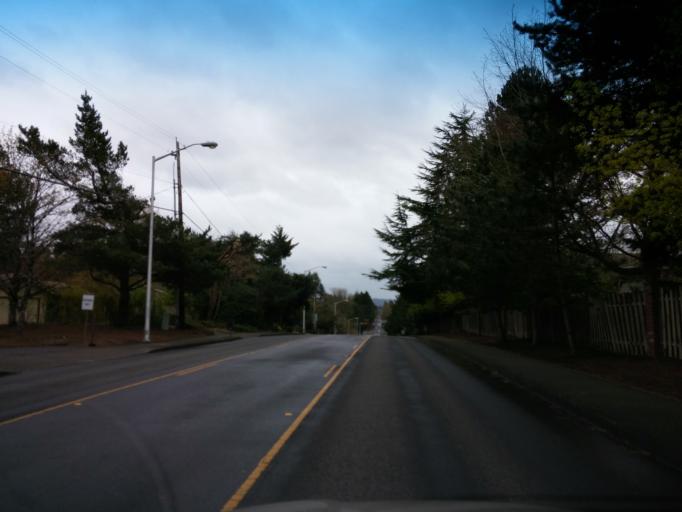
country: US
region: Oregon
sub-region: Washington County
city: Oak Hills
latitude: 45.5298
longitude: -122.8548
